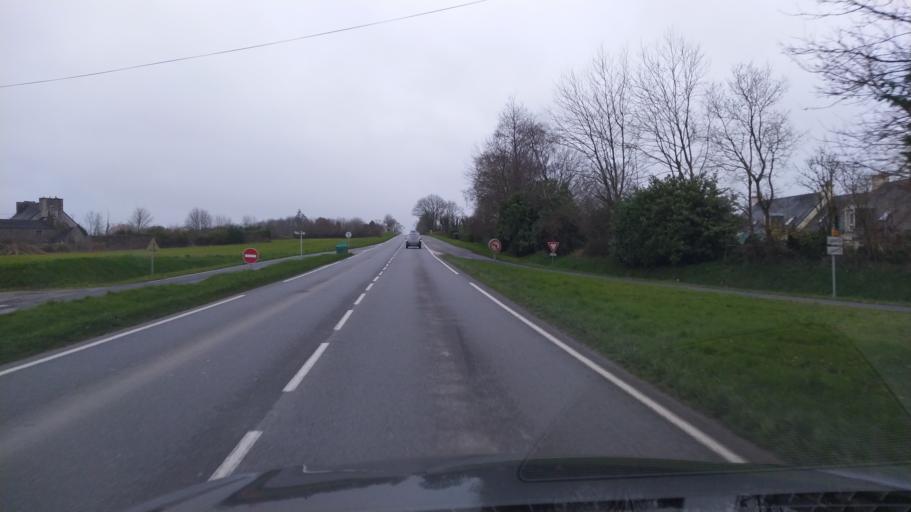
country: FR
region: Brittany
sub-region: Departement du Finistere
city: Landivisiau
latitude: 48.5084
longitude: -4.0555
